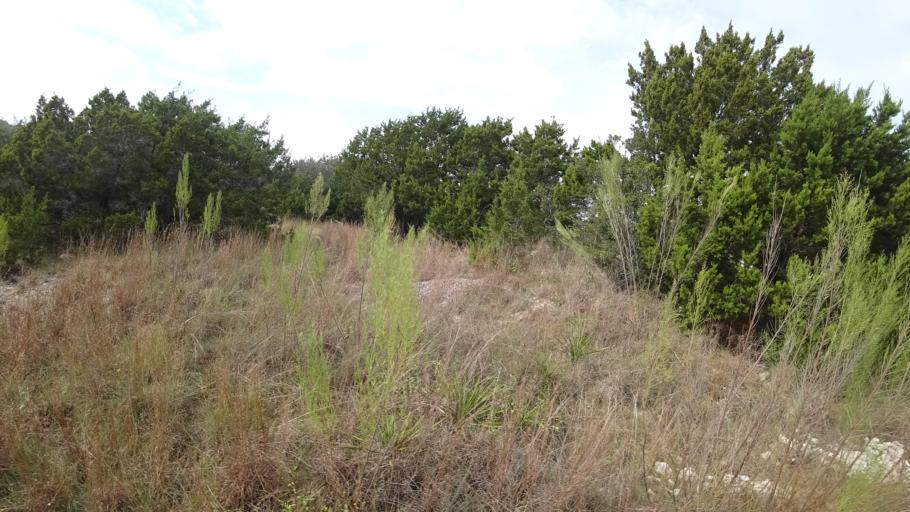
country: US
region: Texas
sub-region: Travis County
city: Hudson Bend
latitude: 30.3734
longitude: -97.9192
